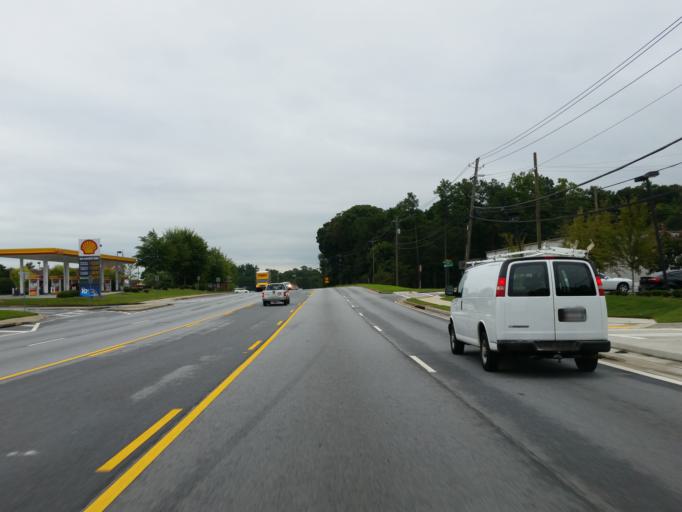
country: US
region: Georgia
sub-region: Cobb County
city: Mableton
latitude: 33.8065
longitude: -84.5300
